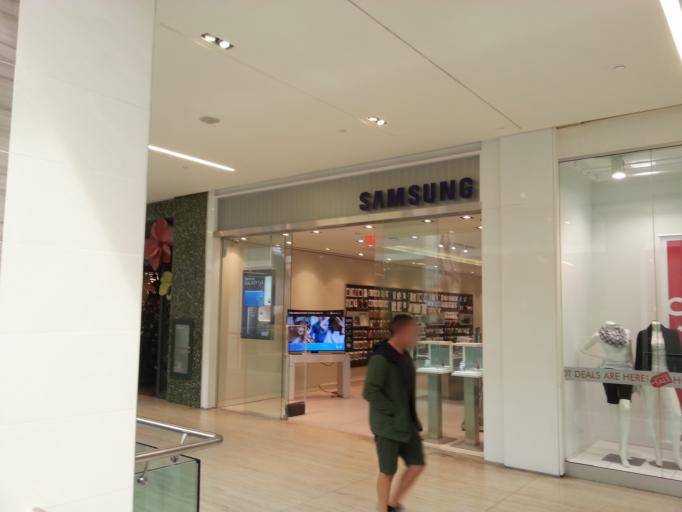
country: CA
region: Alberta
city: St. Albert
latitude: 53.5225
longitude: -113.6211
